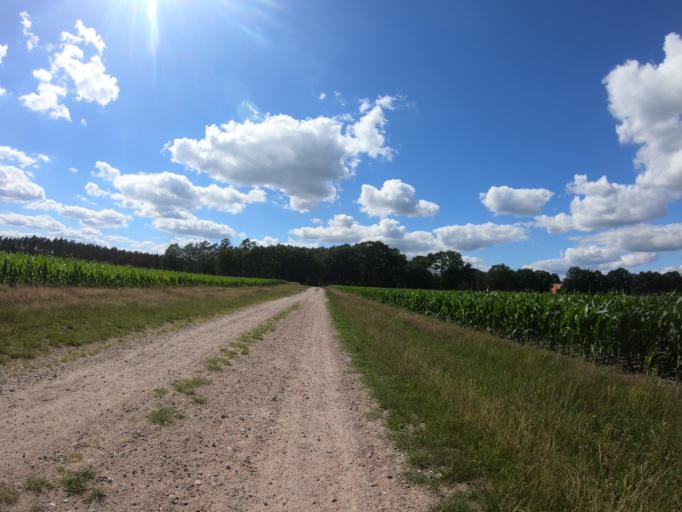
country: DE
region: Lower Saxony
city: Wagenhoff
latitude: 52.5041
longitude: 10.4757
